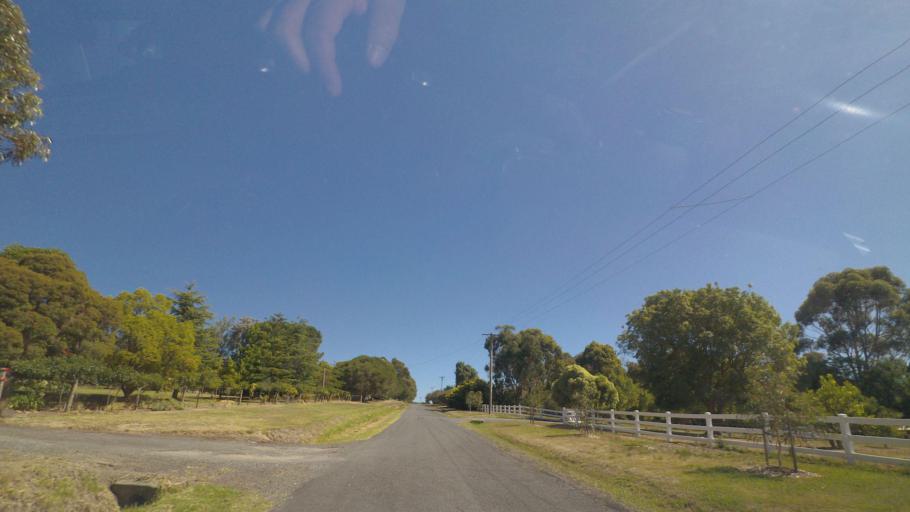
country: AU
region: Victoria
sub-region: Yarra Ranges
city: Chirnside Park
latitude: -37.7377
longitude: 145.3336
